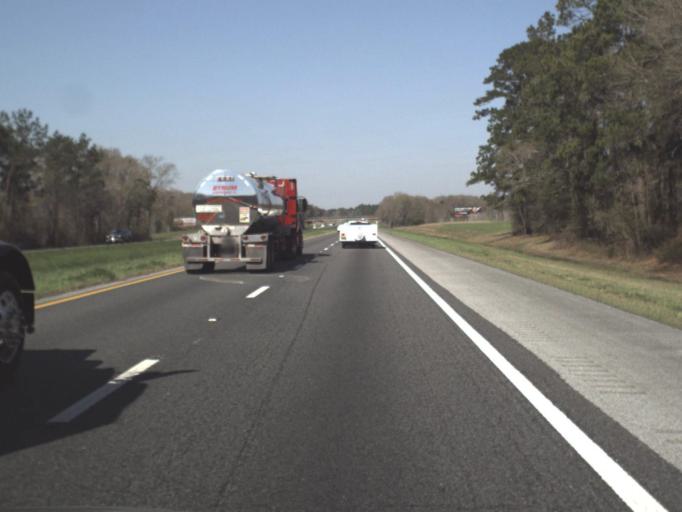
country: US
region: Florida
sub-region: Jackson County
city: Sneads
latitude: 30.6739
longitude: -85.0714
